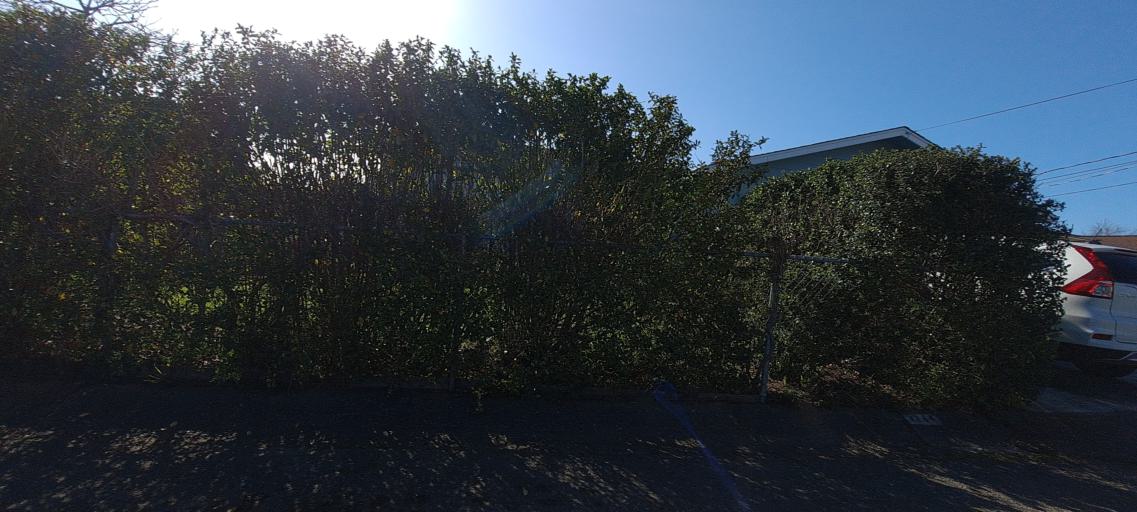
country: US
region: California
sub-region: Humboldt County
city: Fortuna
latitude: 40.5764
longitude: -124.1403
